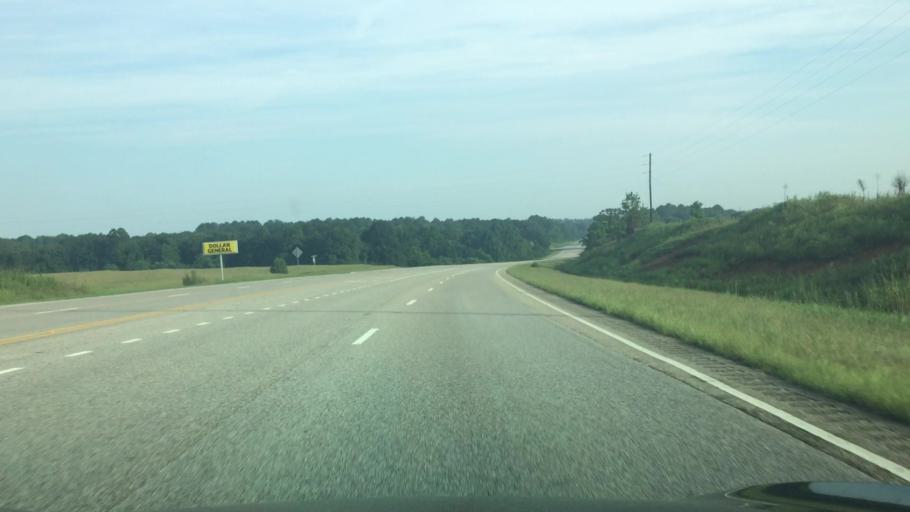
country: US
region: Alabama
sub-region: Covington County
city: Andalusia
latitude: 31.4093
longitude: -86.6045
